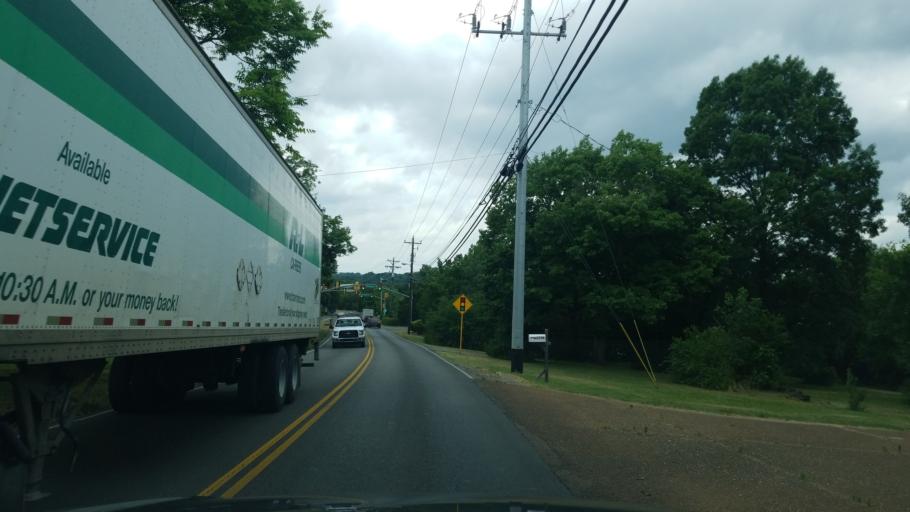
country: US
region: Tennessee
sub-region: Rutherford County
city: La Vergne
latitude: 36.0889
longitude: -86.6129
